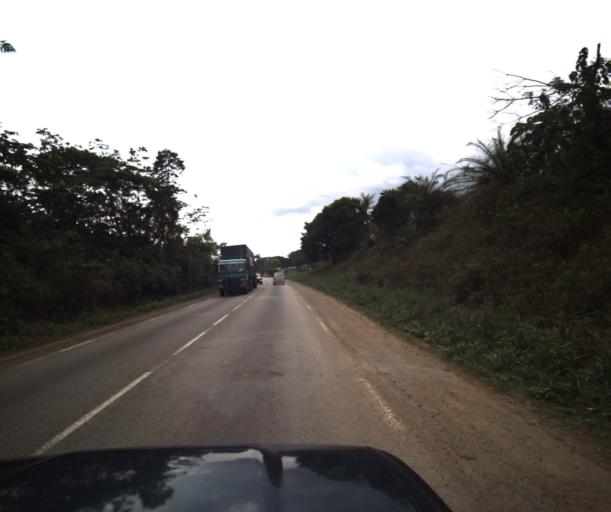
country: CM
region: Littoral
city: Edea
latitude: 3.9503
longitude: 10.0298
